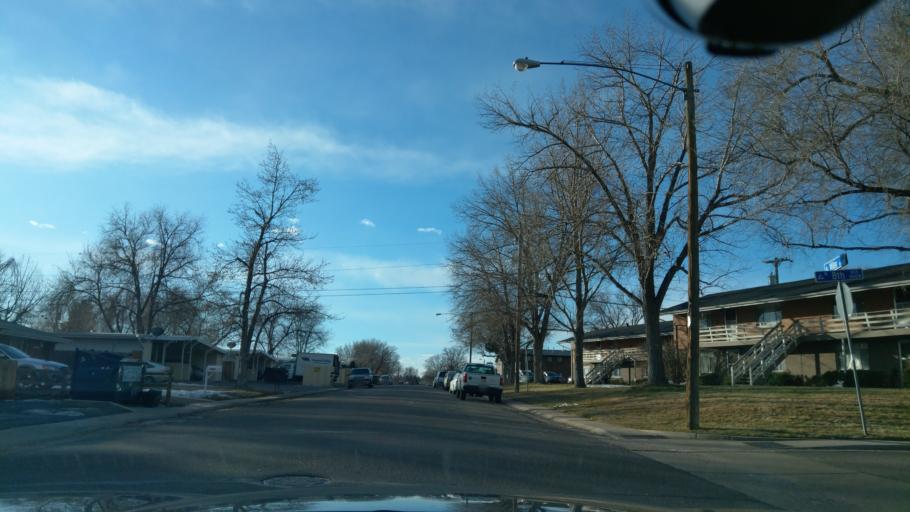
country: US
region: Colorado
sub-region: Jefferson County
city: Lakewood
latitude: 39.7301
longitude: -105.1149
